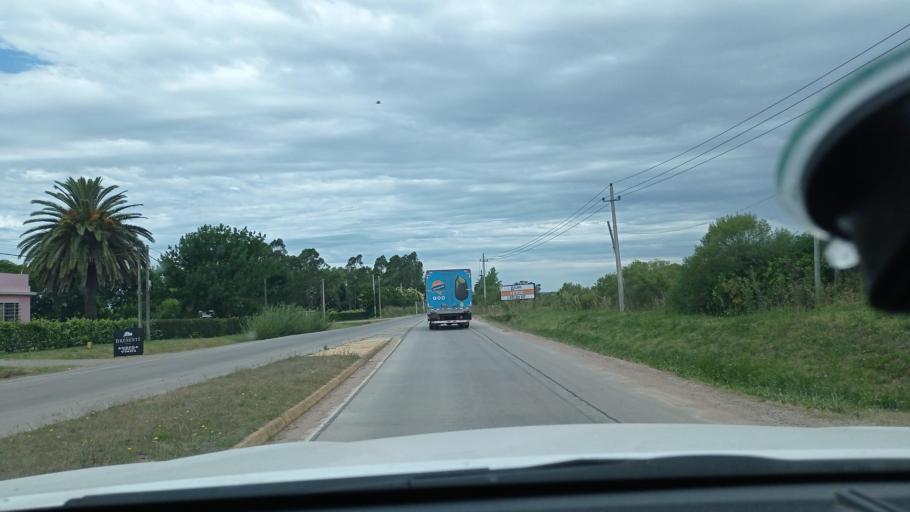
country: UY
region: Canelones
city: La Paz
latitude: -34.7968
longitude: -56.1951
